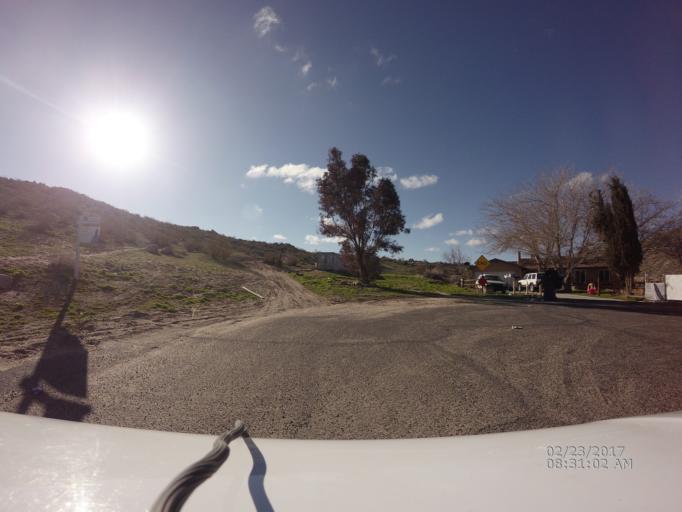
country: US
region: California
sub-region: Los Angeles County
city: Lake Los Angeles
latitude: 34.6090
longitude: -117.8312
